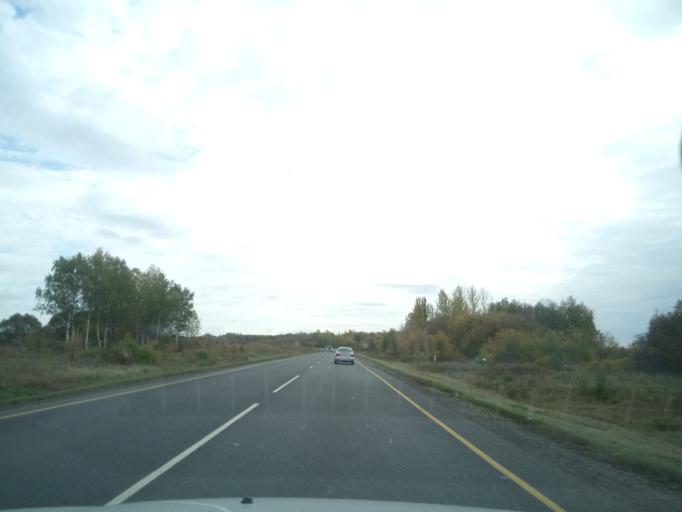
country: RU
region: Nizjnij Novgorod
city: Lukoyanov
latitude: 55.0539
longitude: 44.3717
